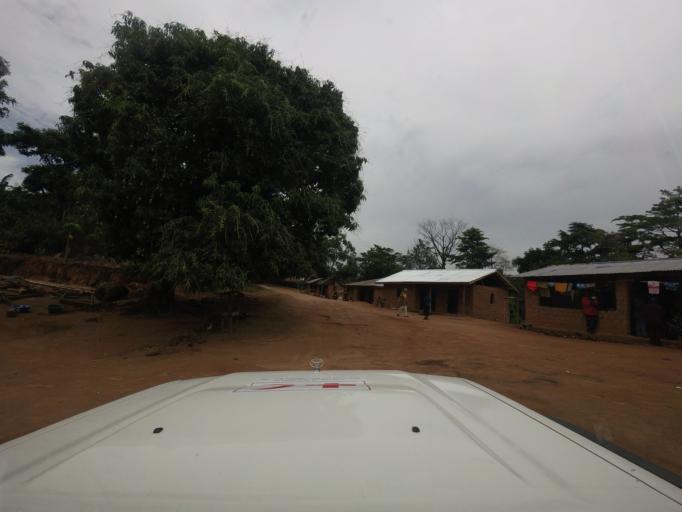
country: SL
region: Eastern Province
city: Buedu
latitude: 8.2450
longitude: -10.2917
